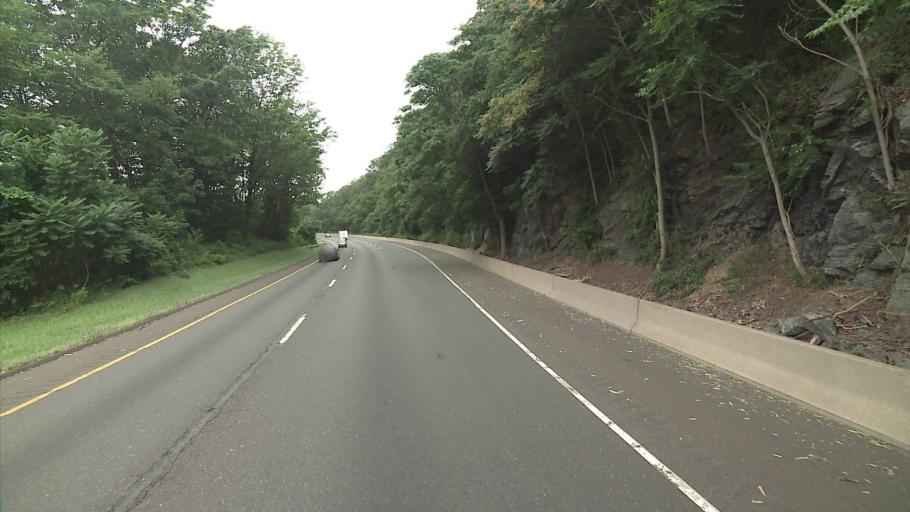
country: US
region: Connecticut
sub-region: Fairfield County
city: Newtown
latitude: 41.4285
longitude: -73.3110
